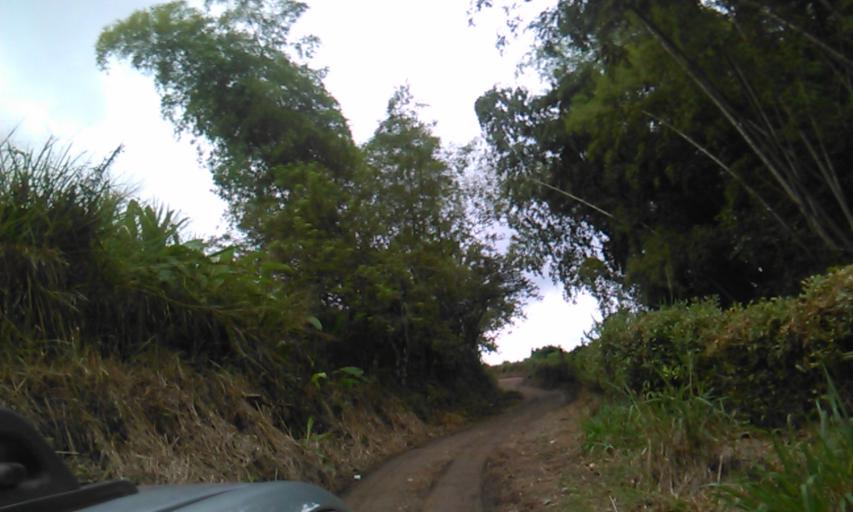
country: CO
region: Quindio
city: La Tebaida
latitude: 4.4983
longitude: -75.8564
